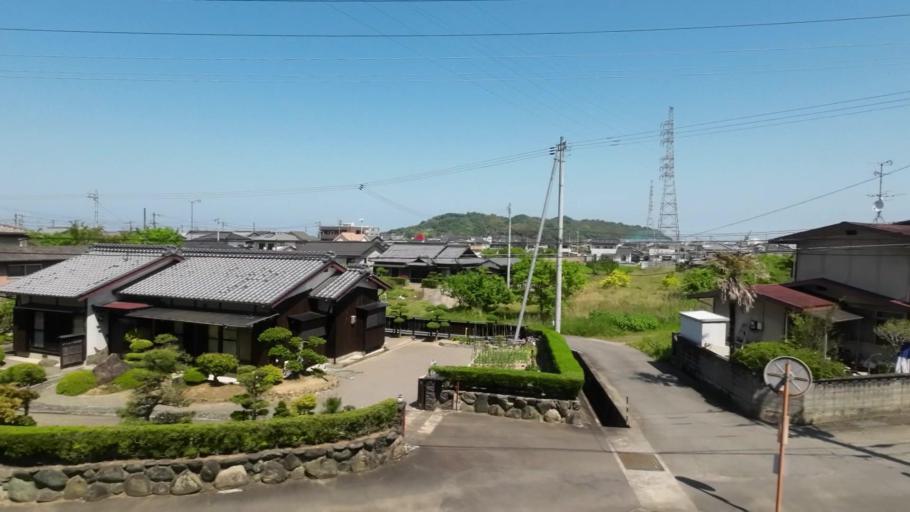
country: JP
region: Ehime
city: Niihama
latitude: 33.9714
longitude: 133.3330
